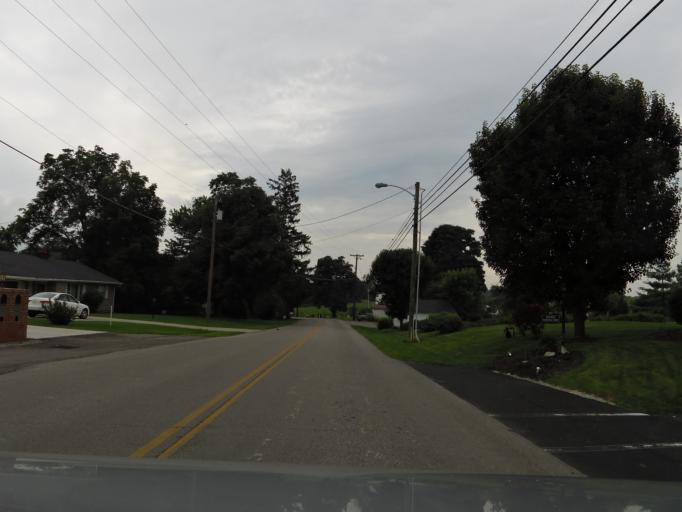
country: US
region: Kentucky
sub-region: Fleming County
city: Flemingsburg
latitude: 38.5203
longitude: -83.8403
